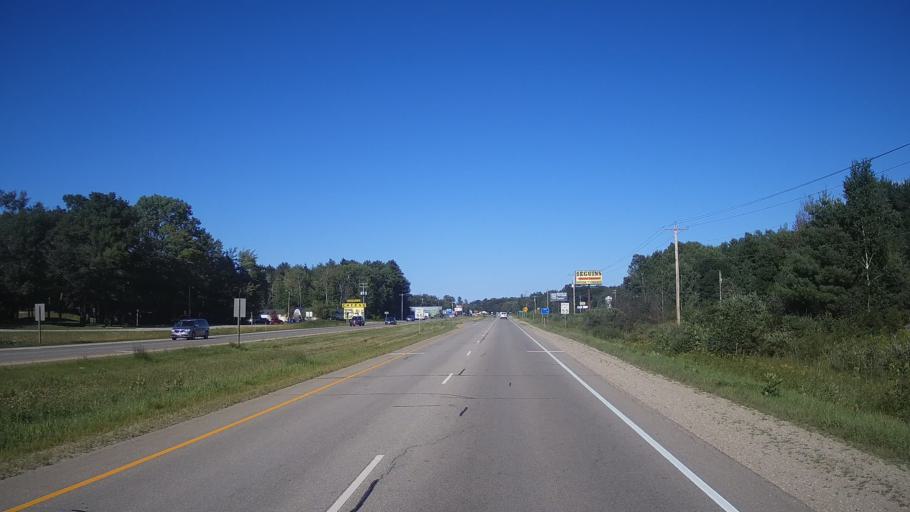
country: US
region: Wisconsin
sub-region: Marinette County
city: Peshtigo
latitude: 45.0647
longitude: -87.6958
